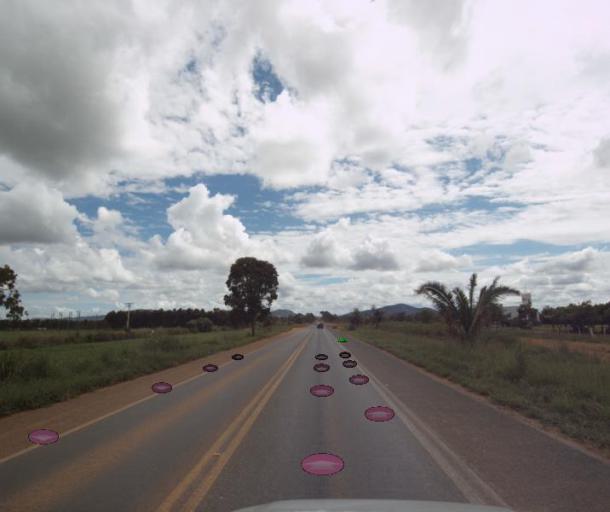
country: BR
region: Goias
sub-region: Uruacu
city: Uruacu
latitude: -14.4658
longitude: -49.1561
